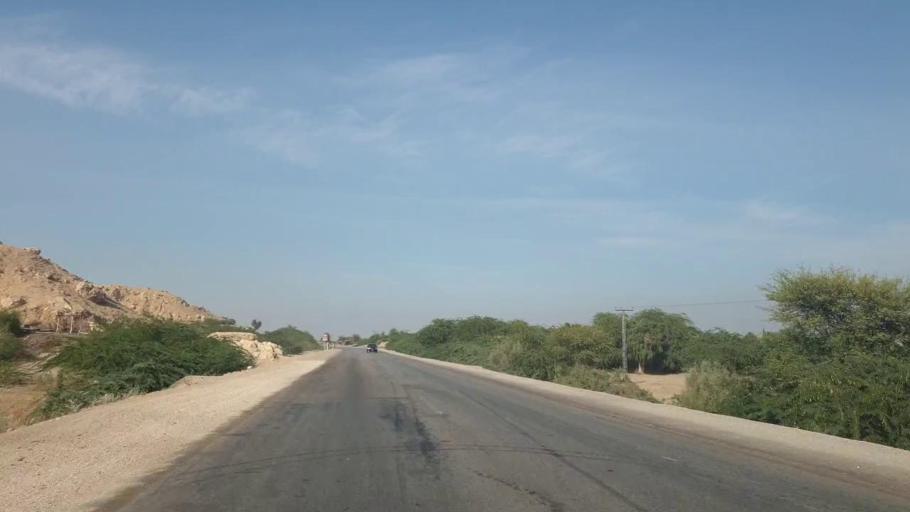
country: PK
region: Sindh
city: Sehwan
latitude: 26.3096
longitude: 67.8925
